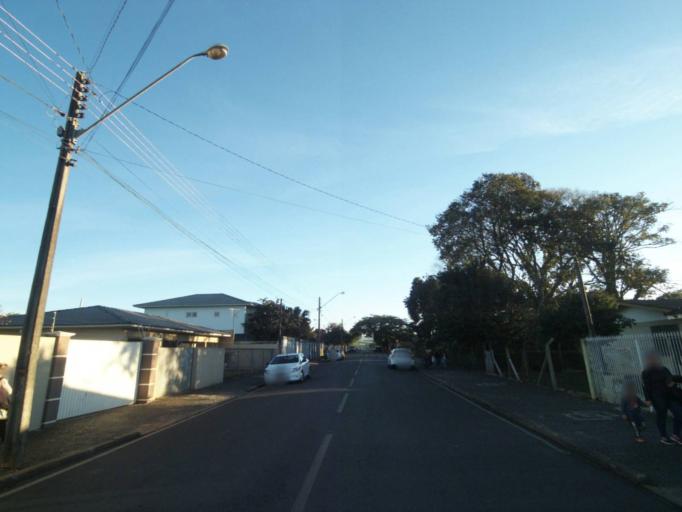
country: BR
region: Parana
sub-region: Tibagi
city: Tibagi
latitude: -24.5118
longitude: -50.4153
